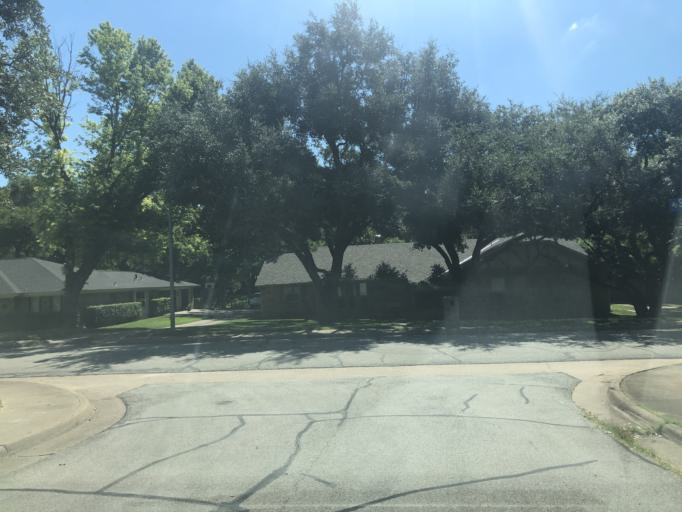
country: US
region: Texas
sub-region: Dallas County
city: Duncanville
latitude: 32.6377
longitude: -96.9268
